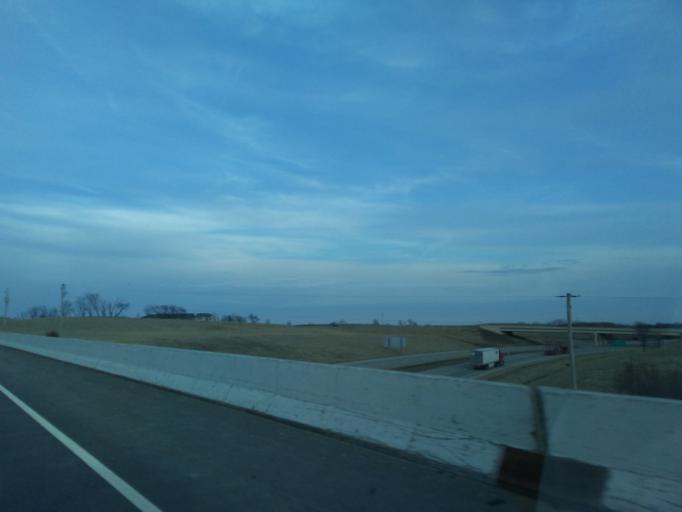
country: US
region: Wisconsin
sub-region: Dane County
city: Verona
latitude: 42.9861
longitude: -89.5621
